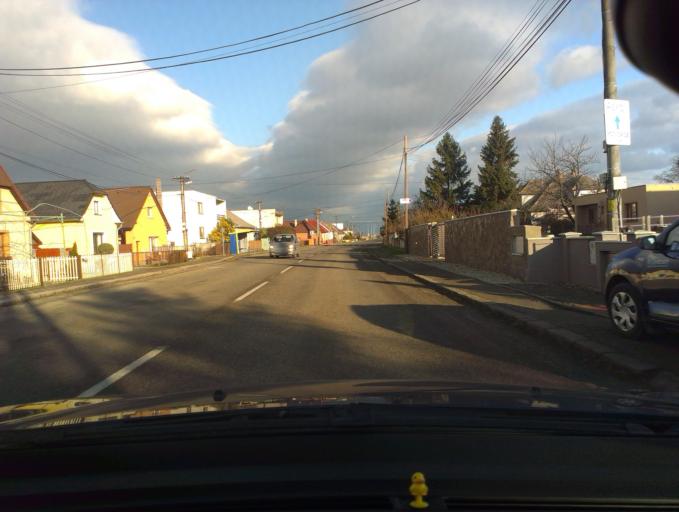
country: SK
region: Nitriansky
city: Cachtice
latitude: 48.6873
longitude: 17.8475
